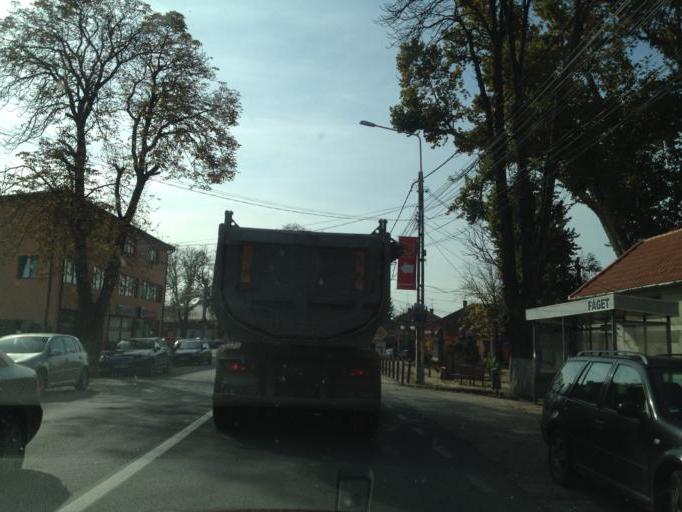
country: RO
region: Timis
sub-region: Comuna Faget
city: Faget
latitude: 45.8563
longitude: 22.1774
